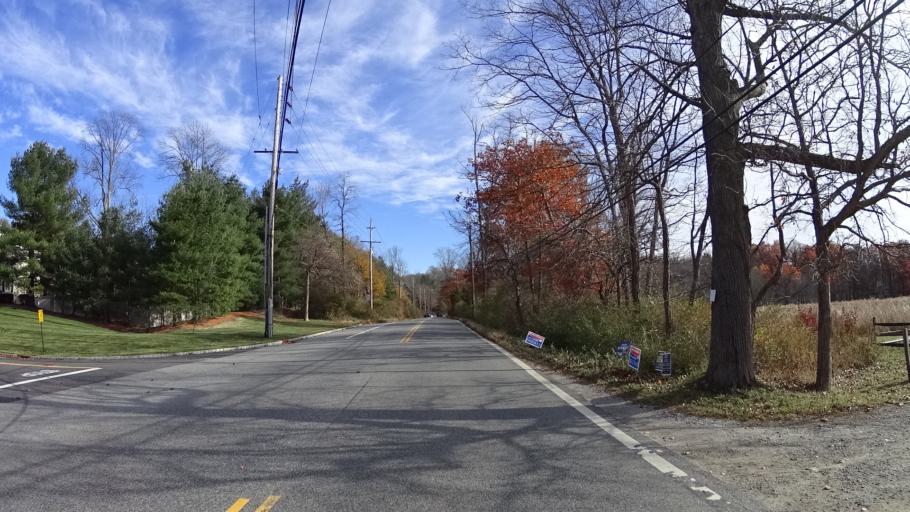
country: US
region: New Jersey
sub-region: Morris County
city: Mendham
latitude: 40.7773
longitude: -74.5791
